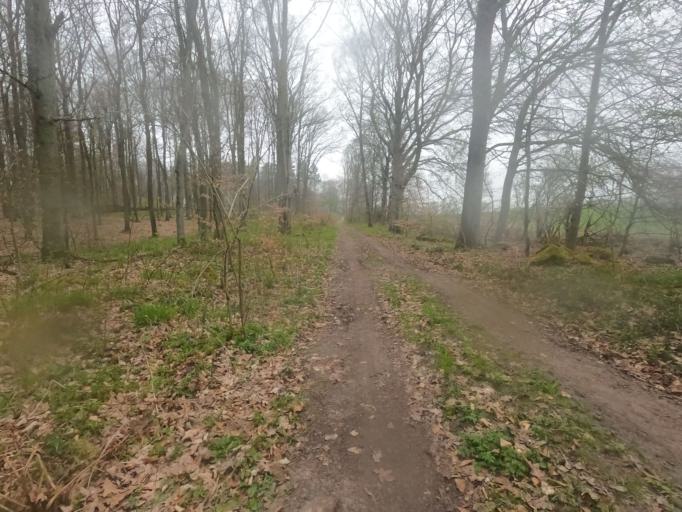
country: PL
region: West Pomeranian Voivodeship
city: Trzcinsko Zdroj
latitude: 52.9255
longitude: 14.7174
